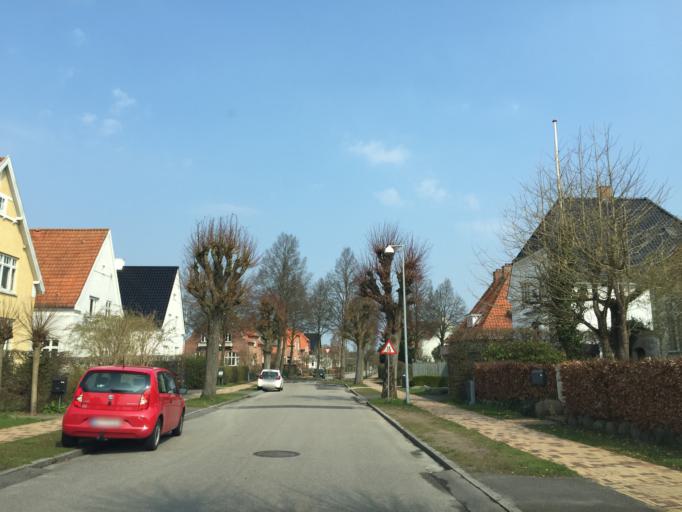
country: DK
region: South Denmark
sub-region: Odense Kommune
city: Odense
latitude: 55.3840
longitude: 10.3812
